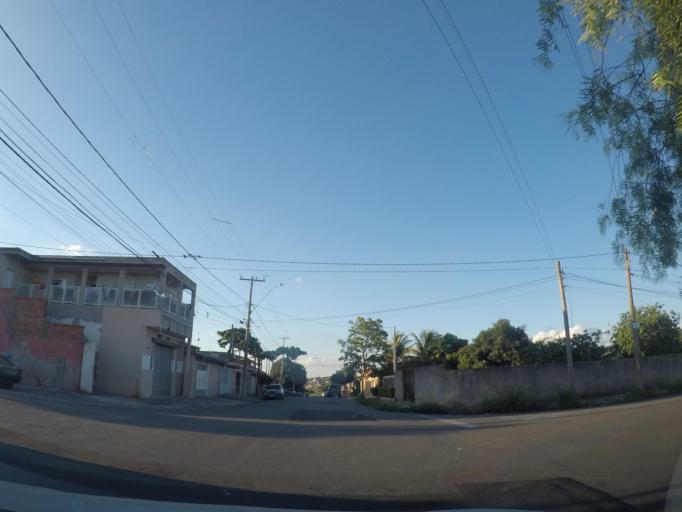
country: BR
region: Sao Paulo
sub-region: Sumare
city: Sumare
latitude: -22.8280
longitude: -47.2469
